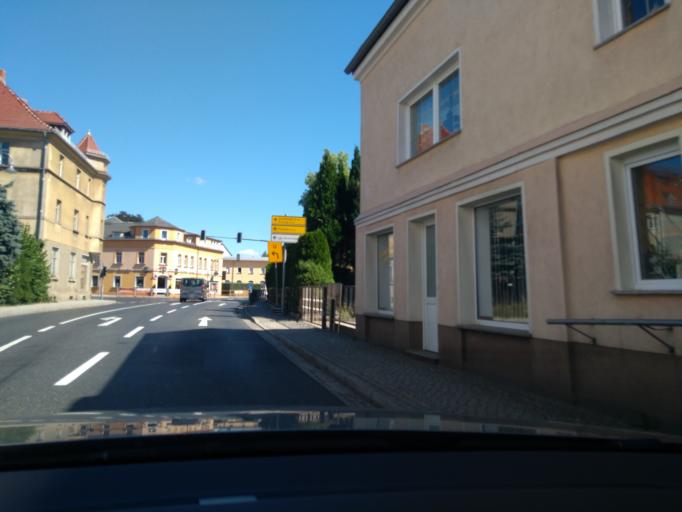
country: DE
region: Saxony
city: Grossrohrsdorf
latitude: 51.1464
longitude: 14.0237
